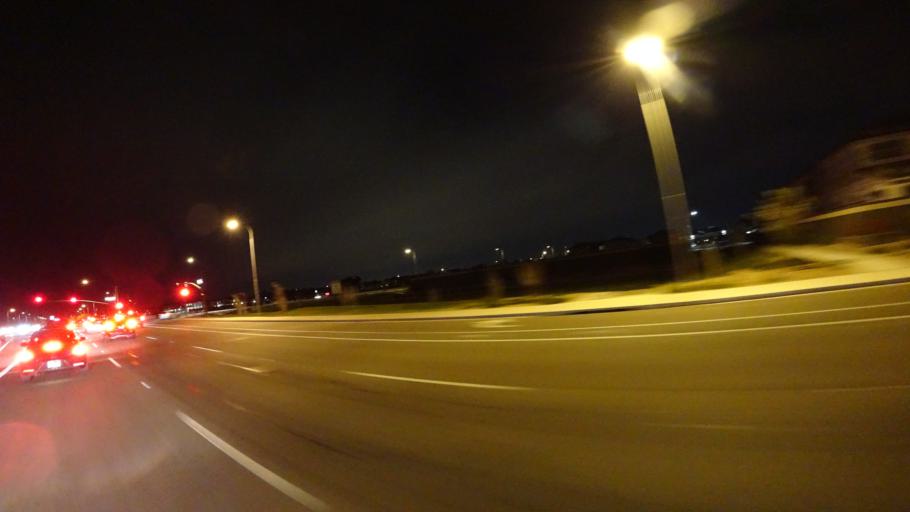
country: US
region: Arizona
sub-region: Maricopa County
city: Chandler
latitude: 33.2622
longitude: -111.8404
